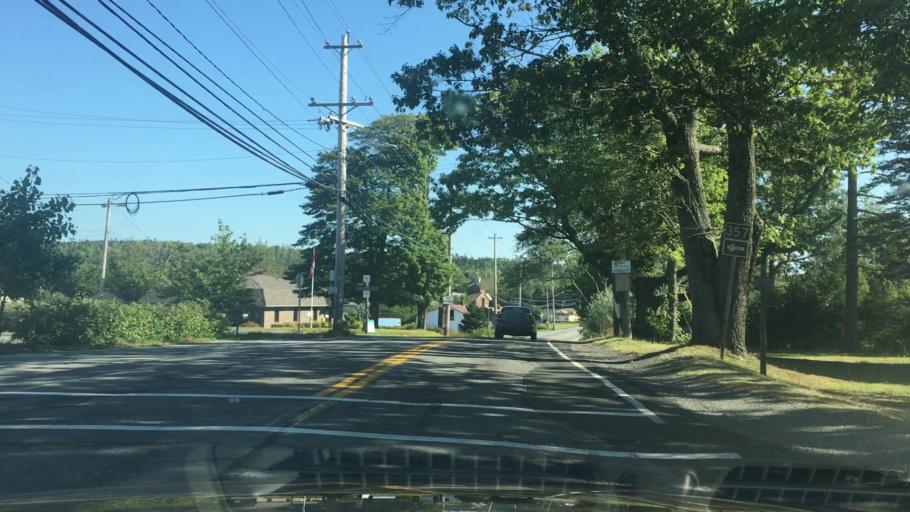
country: CA
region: Nova Scotia
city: Cole Harbour
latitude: 44.7869
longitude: -63.1484
